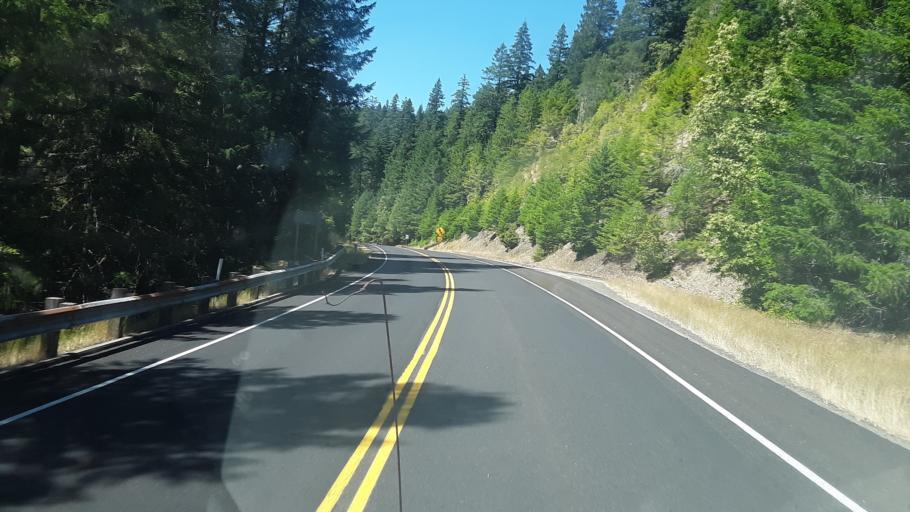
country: US
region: Oregon
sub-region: Josephine County
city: Cave Junction
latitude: 41.9387
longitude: -123.7540
